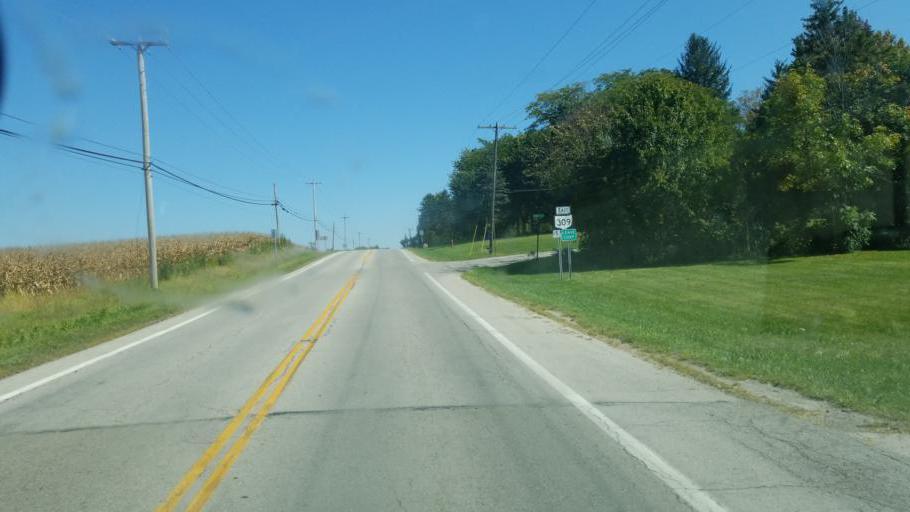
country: US
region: Ohio
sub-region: Crawford County
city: Crestline
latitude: 40.7447
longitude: -82.7454
